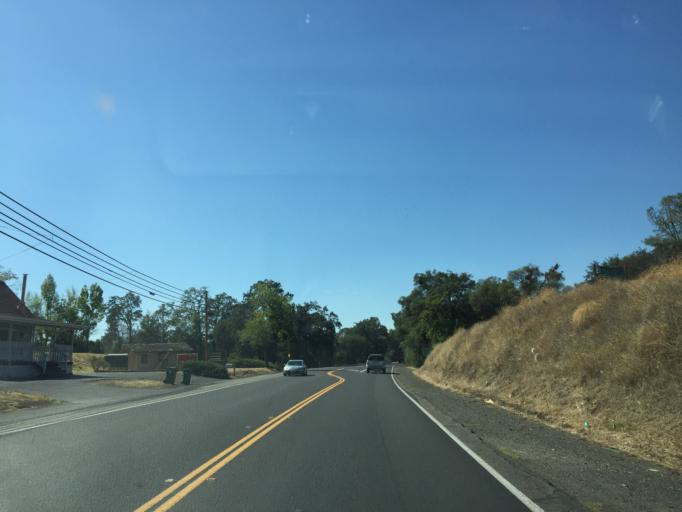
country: US
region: California
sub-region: Tuolumne County
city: Jamestown
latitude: 37.9459
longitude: -120.4268
